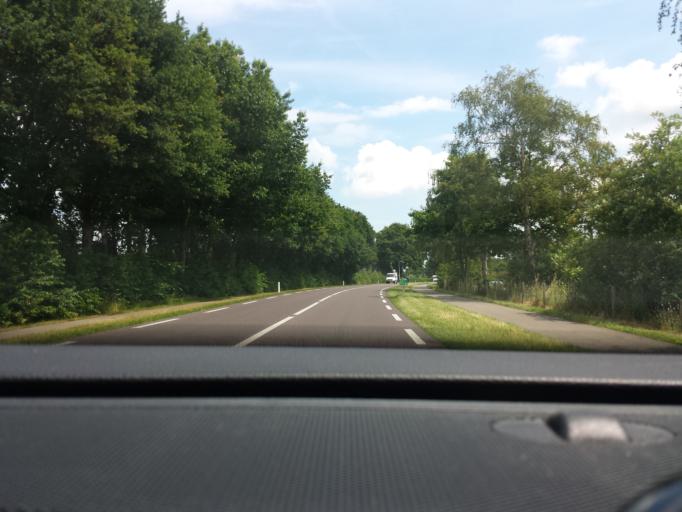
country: NL
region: Gelderland
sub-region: Berkelland
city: Neede
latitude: 52.1375
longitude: 6.5974
